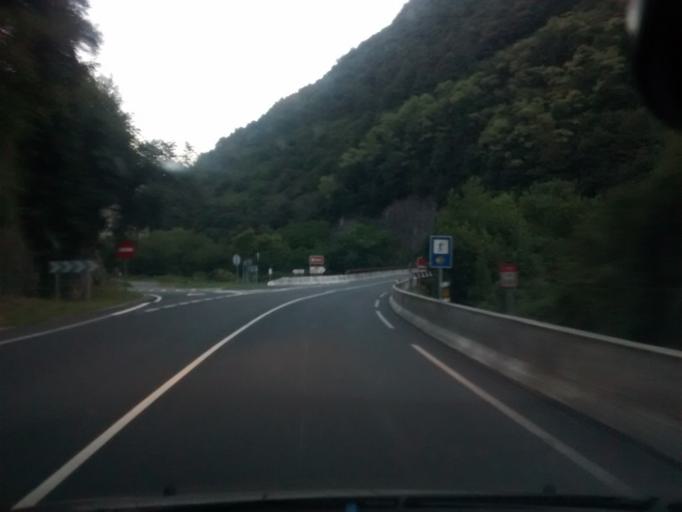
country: ES
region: Basque Country
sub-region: Provincia de Guipuzcoa
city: Mendaro
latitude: 43.2702
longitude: -2.3715
